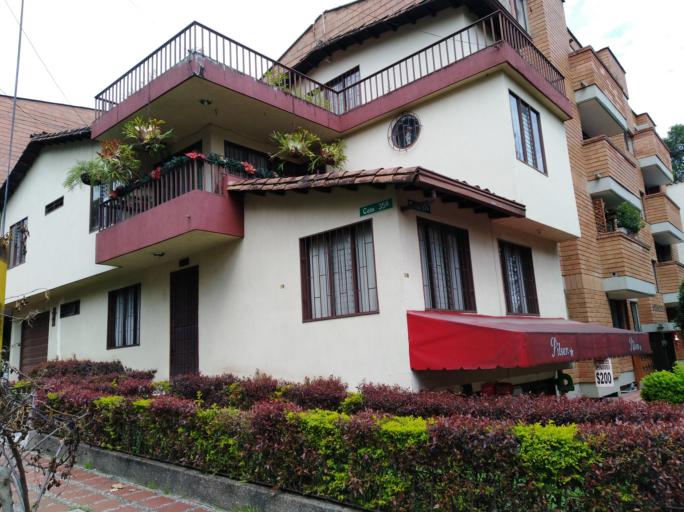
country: CO
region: Antioquia
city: Medellin
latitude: 6.2451
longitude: -75.6117
